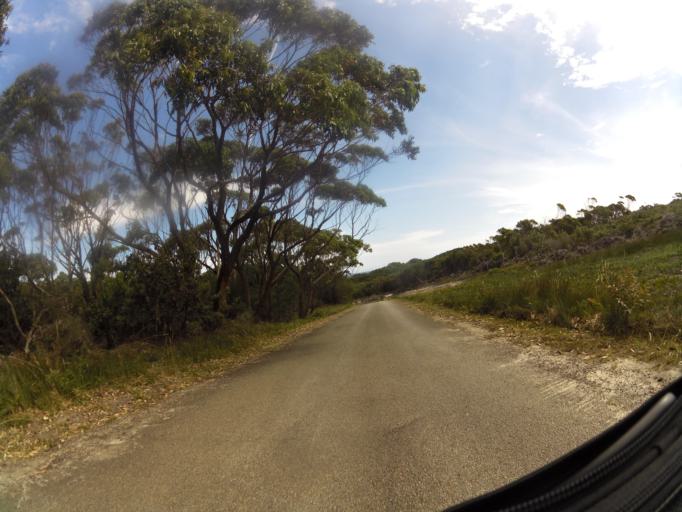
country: AU
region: Victoria
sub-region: East Gippsland
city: Lakes Entrance
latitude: -37.8034
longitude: 148.6348
